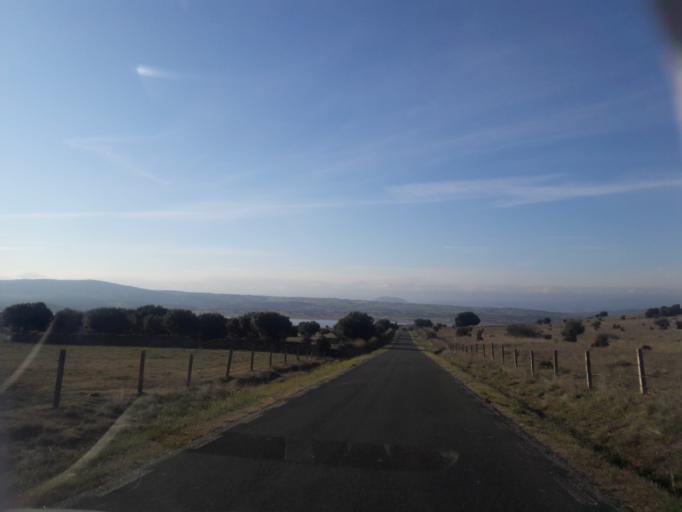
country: ES
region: Castille and Leon
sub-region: Provincia de Salamanca
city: Salvatierra de Tormes
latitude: 40.6025
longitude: -5.6002
